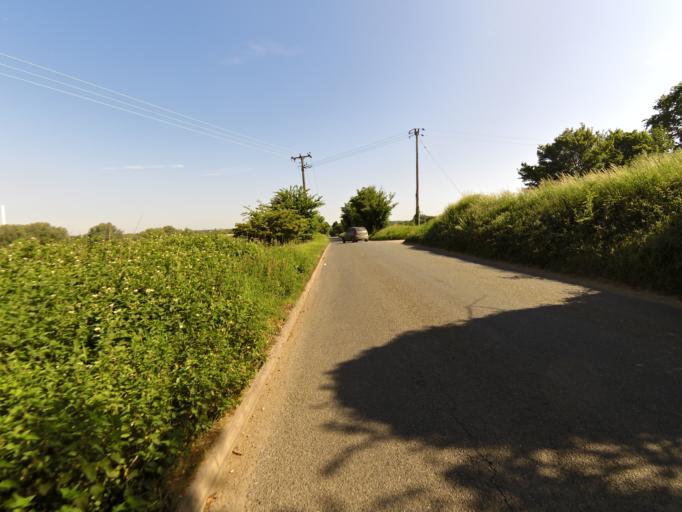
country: GB
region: England
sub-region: Suffolk
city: Bramford
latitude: 52.0964
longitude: 1.1046
